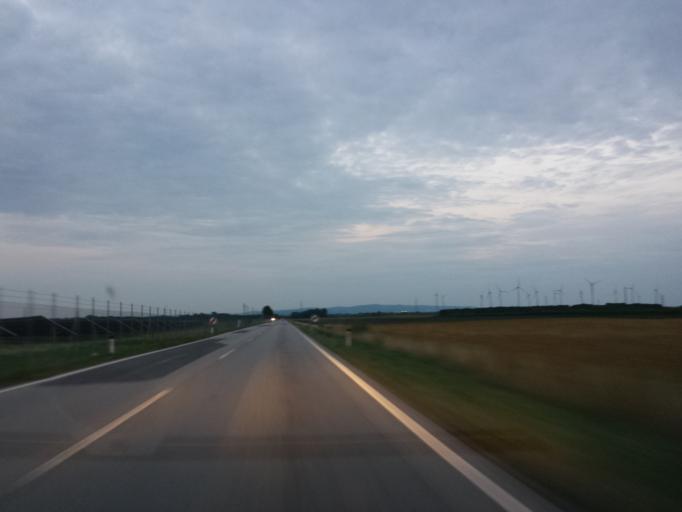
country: AT
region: Lower Austria
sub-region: Politischer Bezirk Baden
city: Oberwaltersdorf
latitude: 47.9701
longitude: 16.3355
